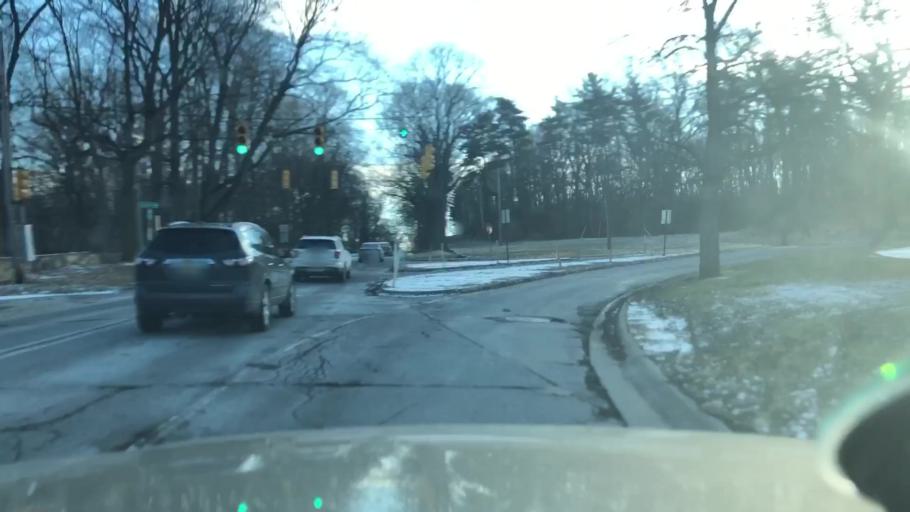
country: US
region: Michigan
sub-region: Jackson County
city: Vandercook Lake
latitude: 42.2150
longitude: -84.4183
